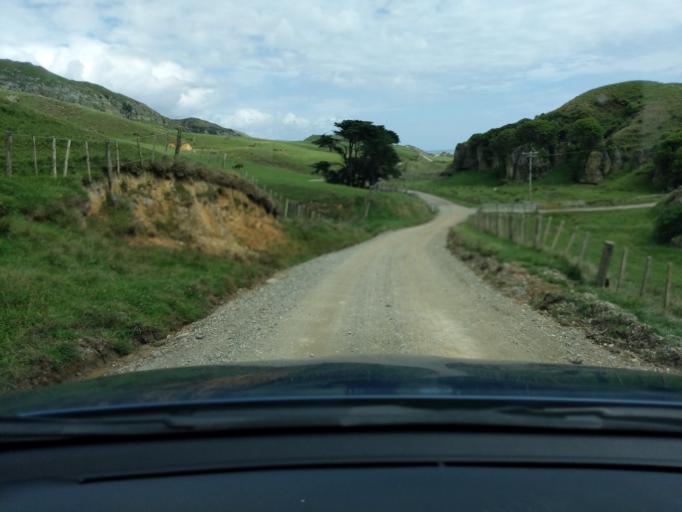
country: NZ
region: Tasman
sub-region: Tasman District
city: Takaka
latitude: -40.6496
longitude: 172.4254
